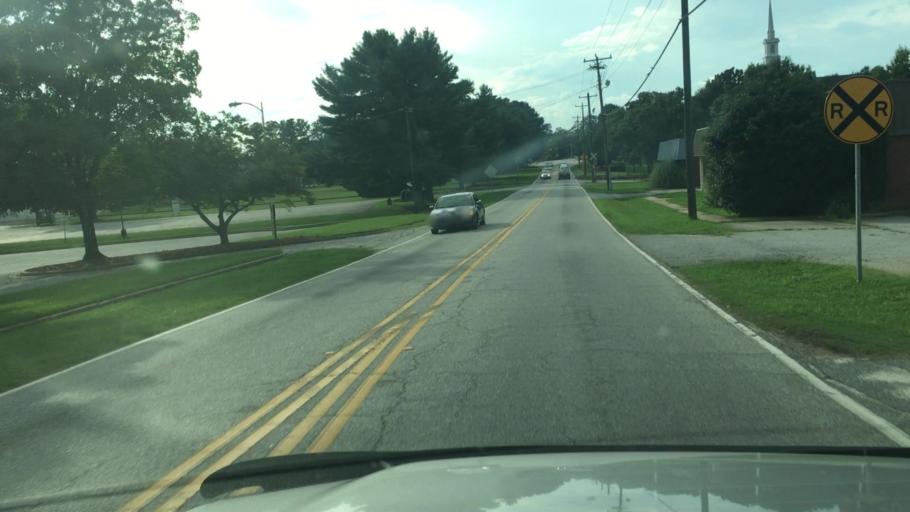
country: US
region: South Carolina
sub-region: Spartanburg County
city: Spartanburg
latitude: 34.9734
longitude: -81.9305
